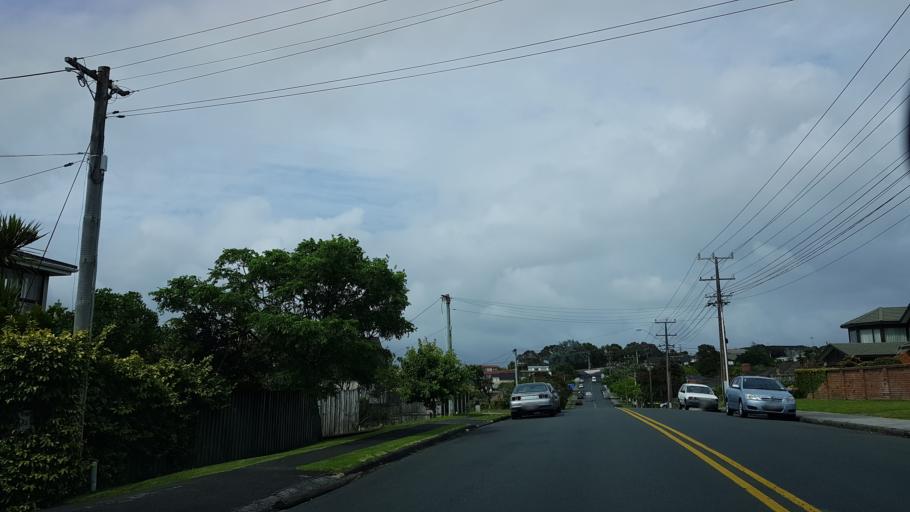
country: NZ
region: Auckland
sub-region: Auckland
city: North Shore
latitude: -36.7987
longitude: 174.7395
